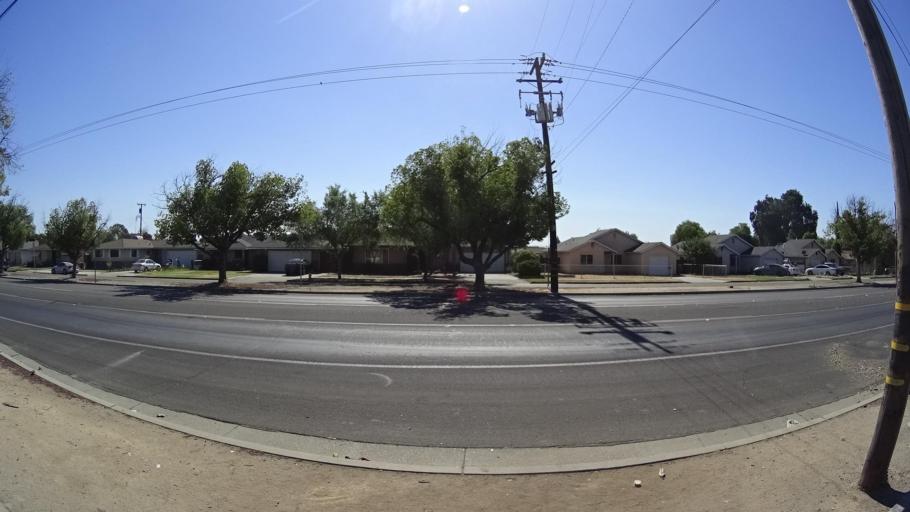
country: US
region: California
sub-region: Fresno County
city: West Park
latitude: 36.7757
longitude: -119.8357
